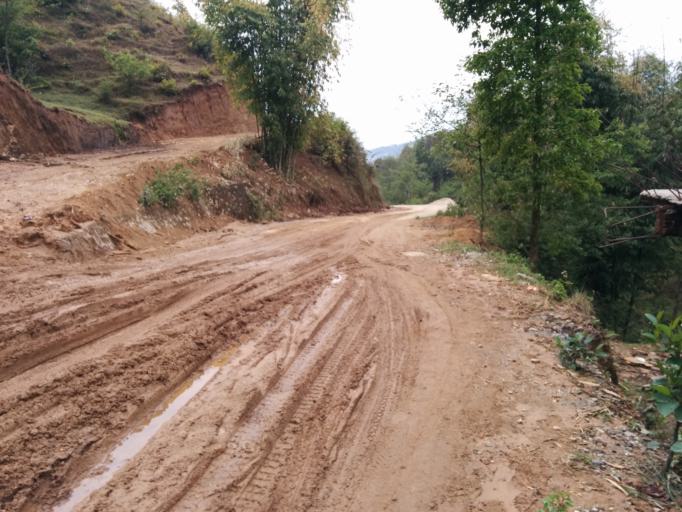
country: NP
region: Central Region
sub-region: Bagmati Zone
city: Nagarkot
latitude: 27.7630
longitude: 85.4968
